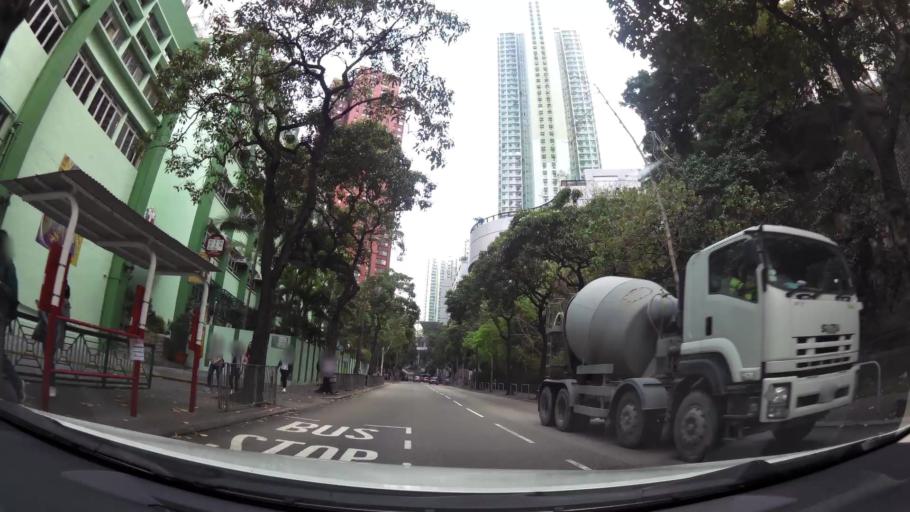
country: HK
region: Kowloon City
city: Kowloon
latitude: 22.3062
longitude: 114.2355
